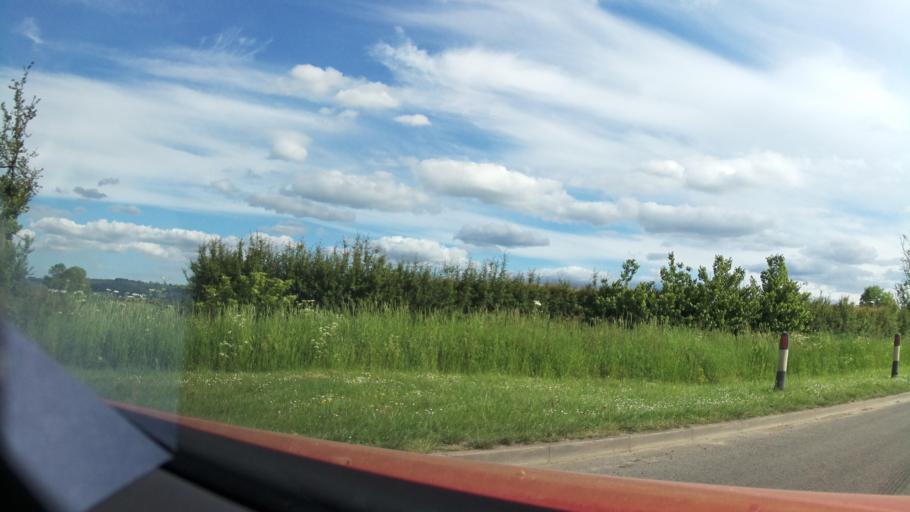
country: GB
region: England
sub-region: Worcestershire
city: Badsey
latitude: 52.0875
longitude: -1.8584
